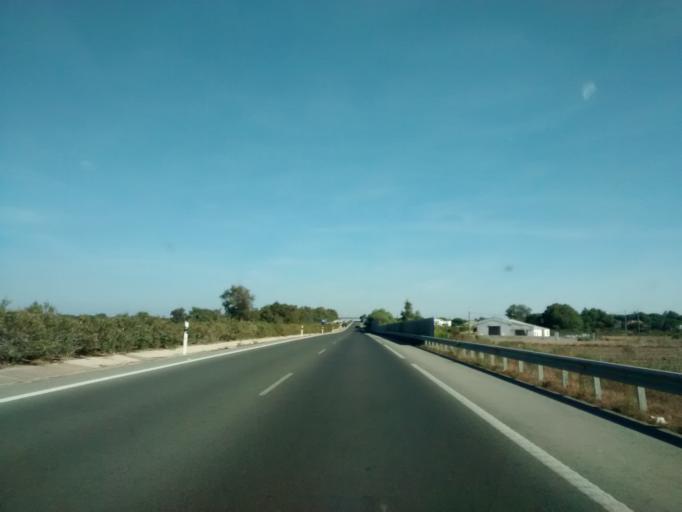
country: ES
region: Andalusia
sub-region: Provincia de Cadiz
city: Chiclana de la Frontera
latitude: 36.3708
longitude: -6.1129
